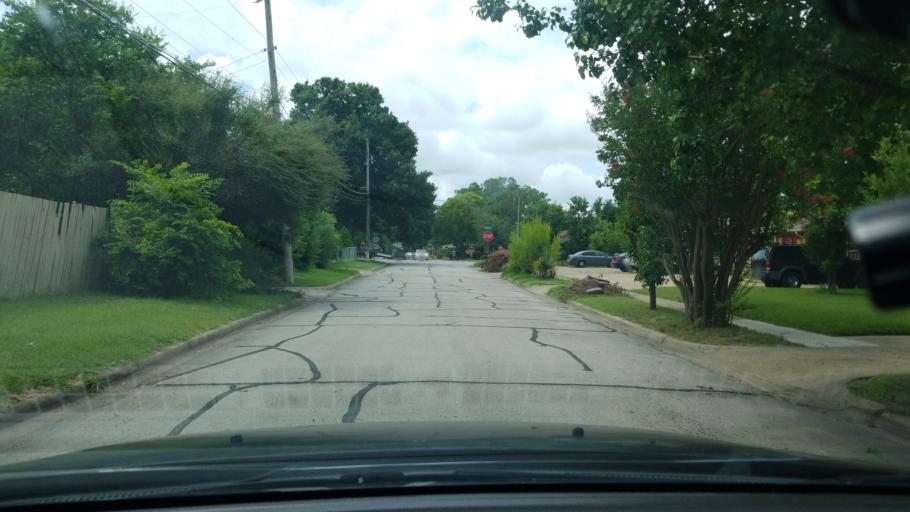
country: US
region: Texas
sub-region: Dallas County
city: Mesquite
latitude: 32.8222
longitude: -96.6745
